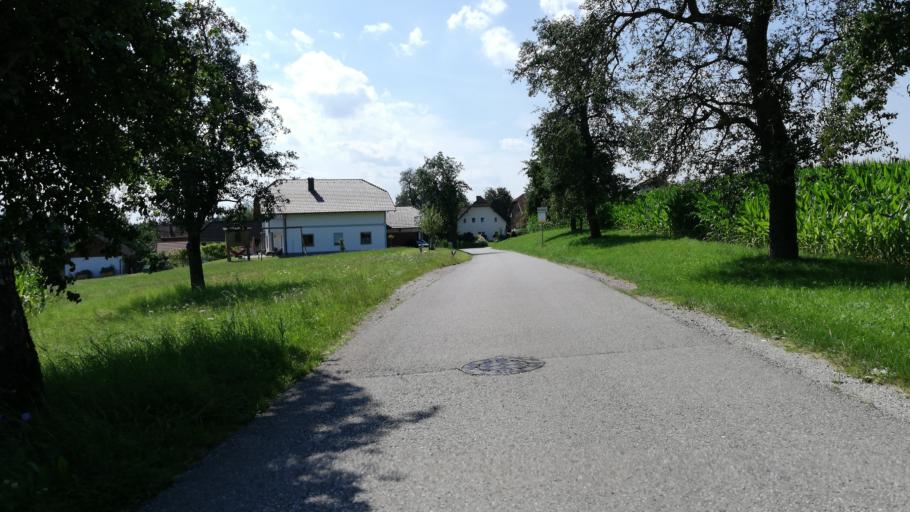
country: AT
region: Upper Austria
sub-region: Wels-Land
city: Gunskirchen
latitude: 48.1720
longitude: 13.9070
